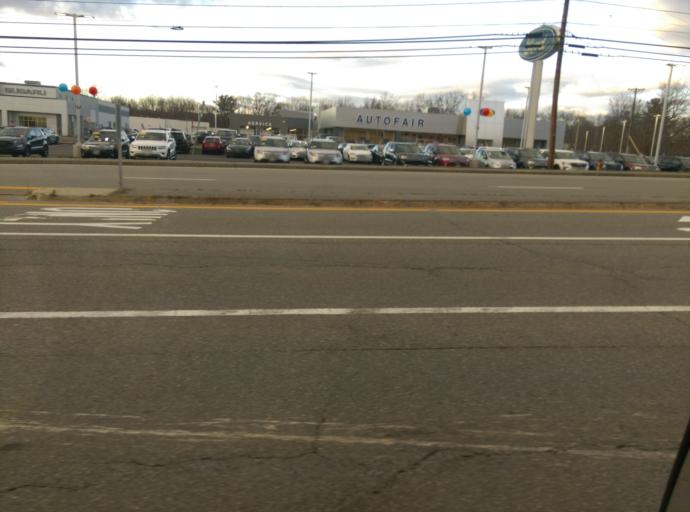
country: US
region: Massachusetts
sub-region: Essex County
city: Haverhill
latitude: 42.7838
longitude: -71.1185
